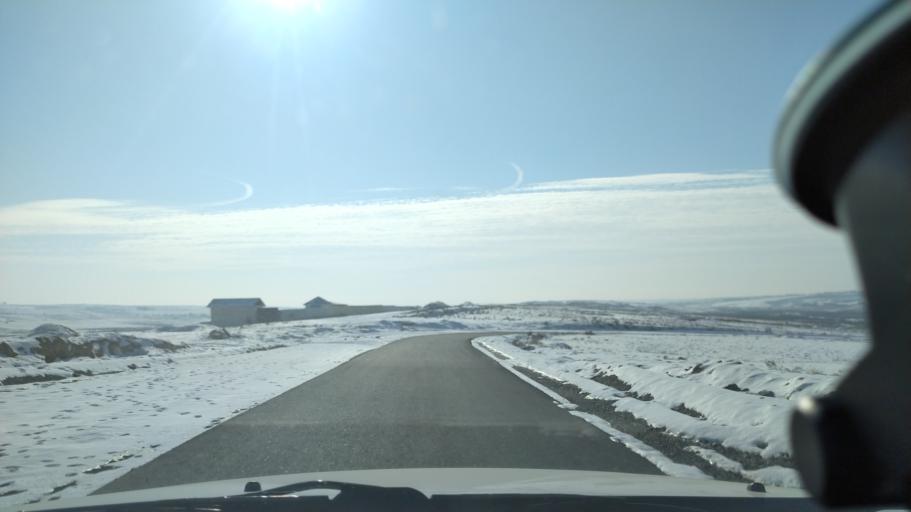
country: UZ
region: Namangan
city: Yangiqo`rg`on
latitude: 41.1381
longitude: 71.6575
